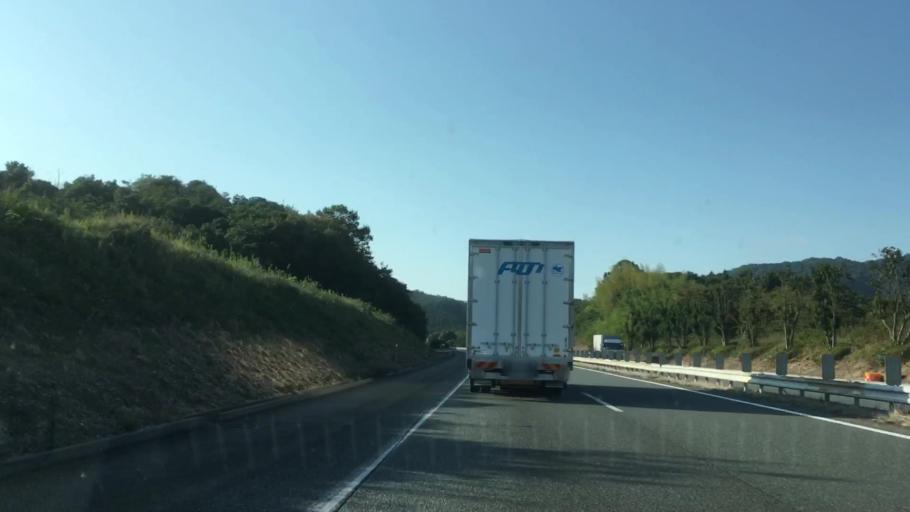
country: JP
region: Yamaguchi
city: Hofu
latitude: 34.0738
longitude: 131.4945
